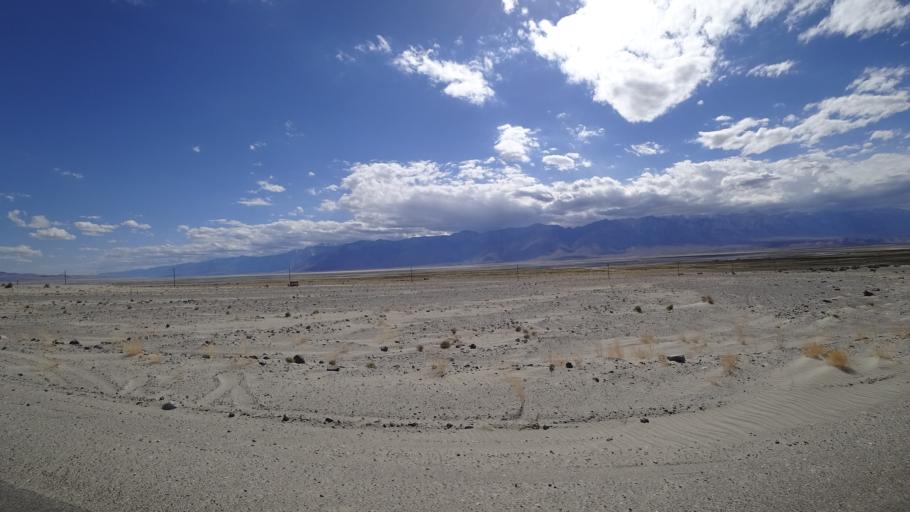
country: US
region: California
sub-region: Inyo County
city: Lone Pine
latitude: 36.5166
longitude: -117.8985
